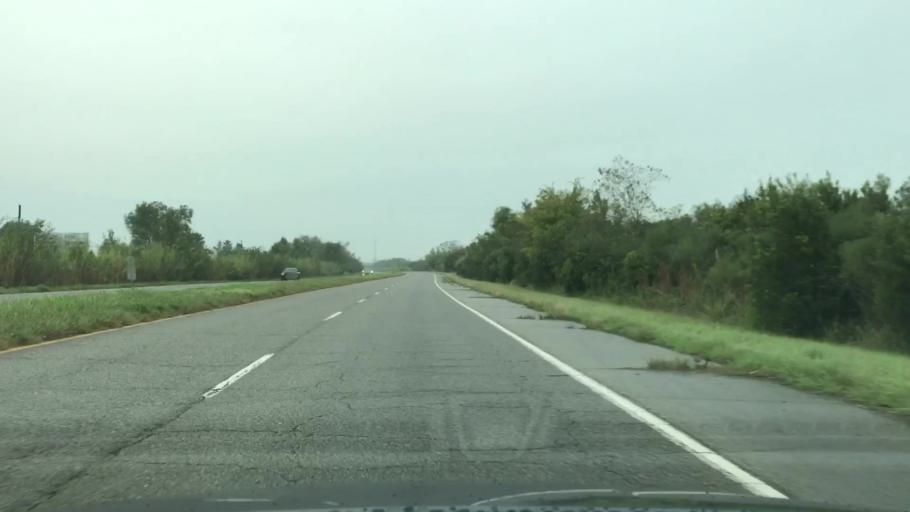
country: US
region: Louisiana
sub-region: Saint Charles Parish
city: Des Allemands
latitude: 29.7979
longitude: -90.5057
